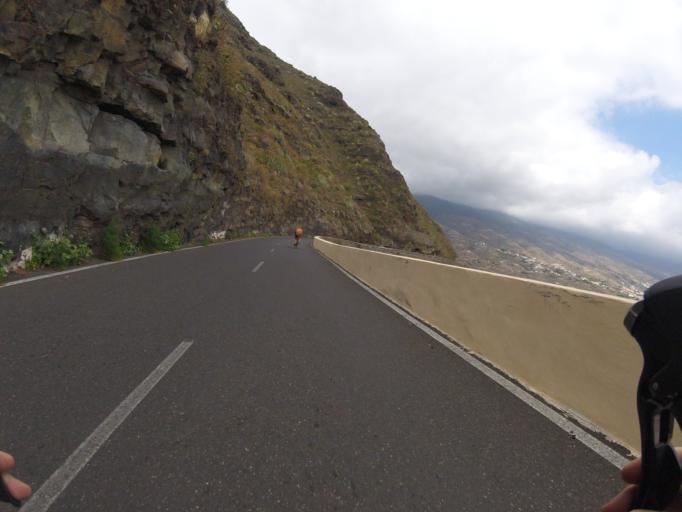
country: ES
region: Canary Islands
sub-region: Provincia de Santa Cruz de Tenerife
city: Guimar
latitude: 28.2940
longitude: -16.4080
